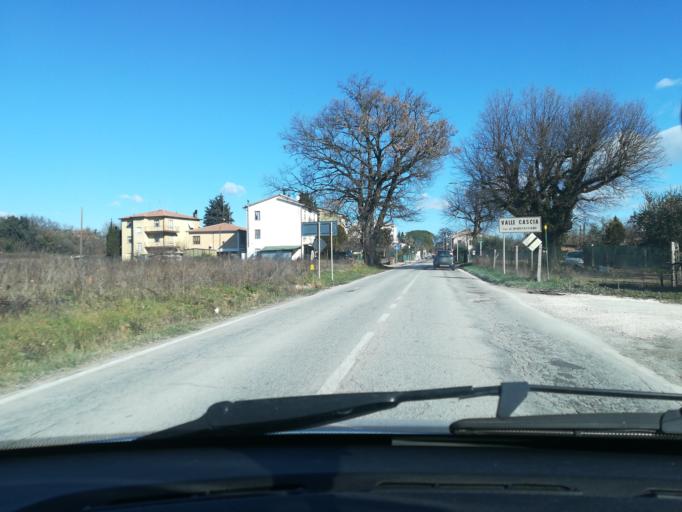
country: IT
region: The Marches
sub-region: Provincia di Macerata
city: Montecassiano
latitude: 43.3438
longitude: 13.4324
